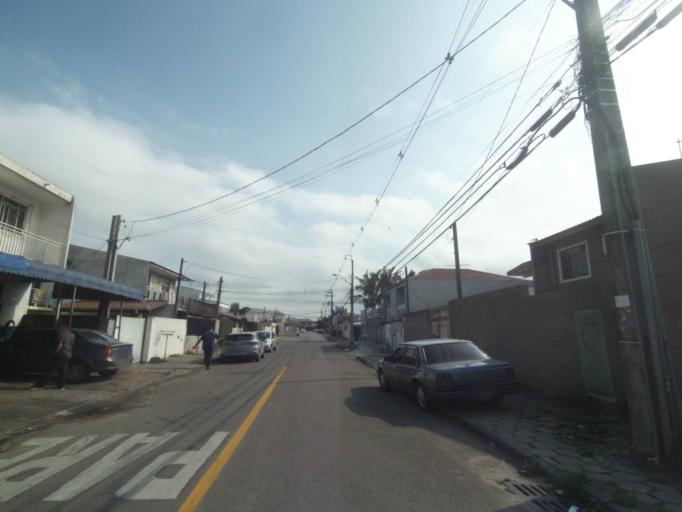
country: BR
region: Parana
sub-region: Sao Jose Dos Pinhais
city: Sao Jose dos Pinhais
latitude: -25.5383
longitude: -49.2601
